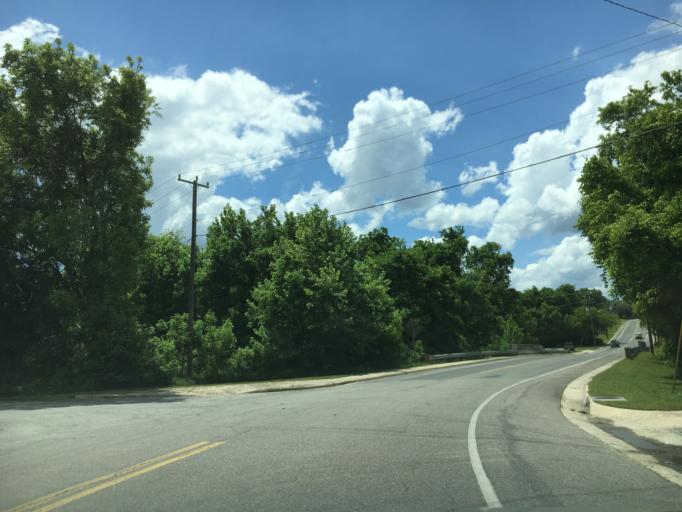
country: US
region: Virginia
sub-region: Halifax County
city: South Boston
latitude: 36.6983
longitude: -78.9133
